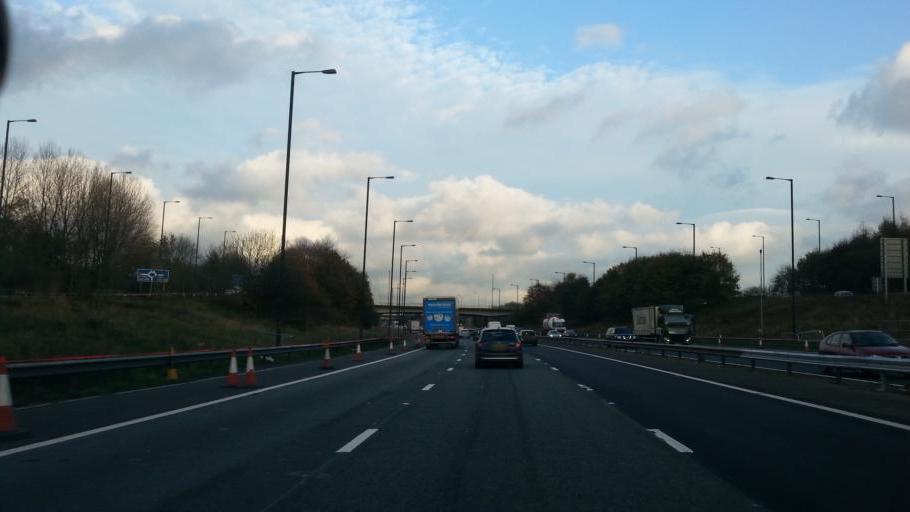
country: GB
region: England
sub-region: Borough of Rochdale
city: Rochdale
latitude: 53.5860
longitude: -2.1633
